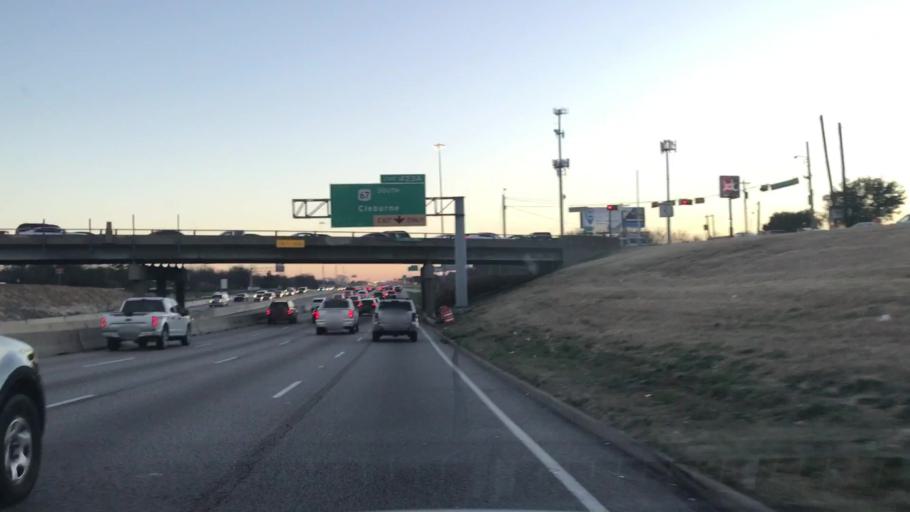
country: US
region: Texas
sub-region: Dallas County
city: Cockrell Hill
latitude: 32.7211
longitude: -96.8276
